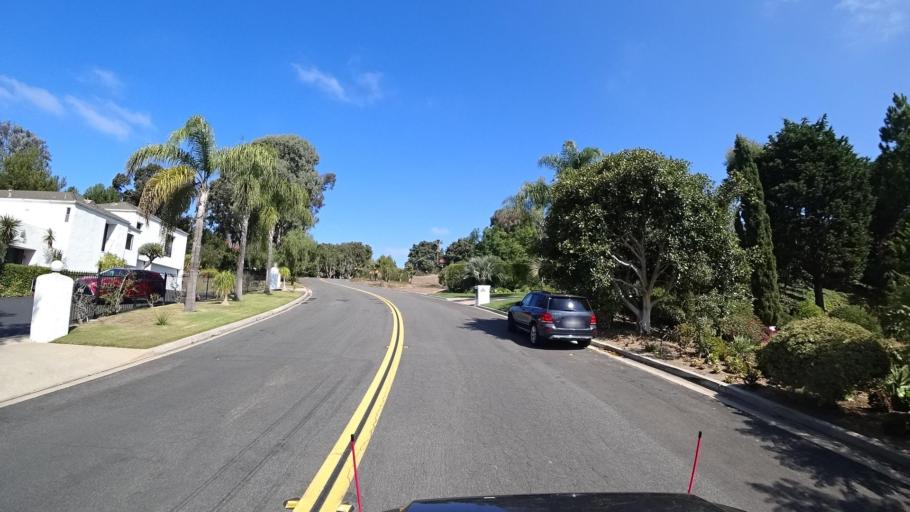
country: US
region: California
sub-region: San Diego County
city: Solana Beach
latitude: 32.9849
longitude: -117.2343
